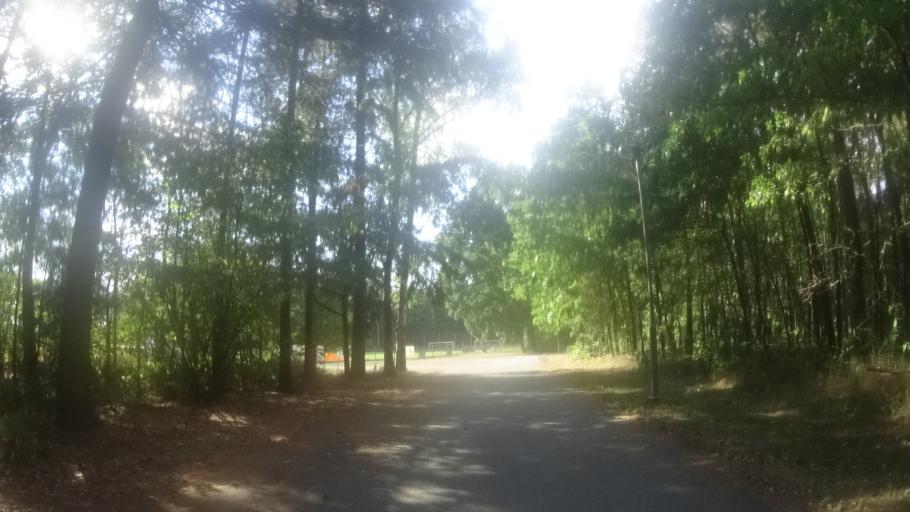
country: CZ
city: Albrechtice nad Orlici
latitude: 50.1757
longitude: 16.0340
